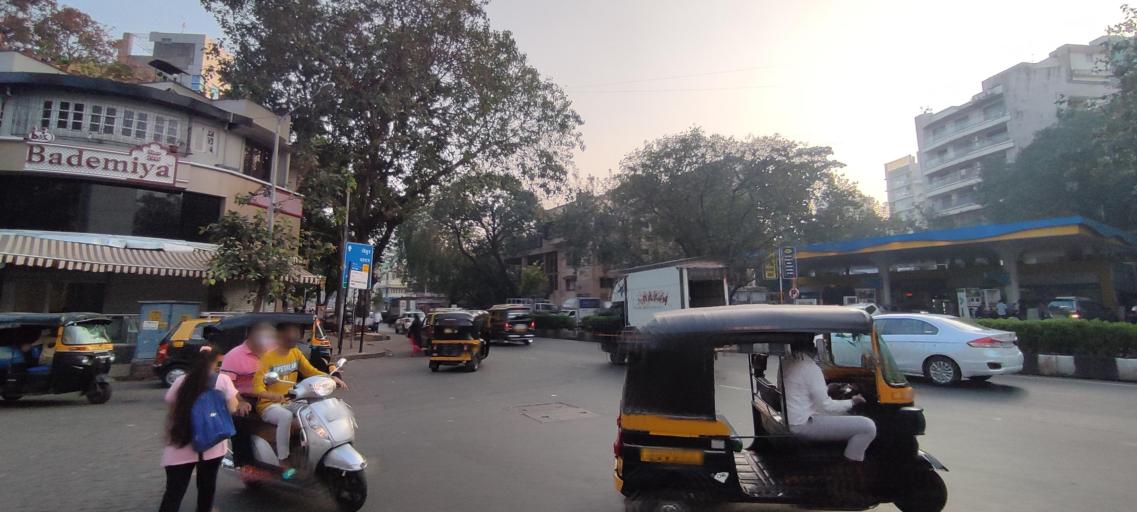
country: IN
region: Maharashtra
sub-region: Mumbai Suburban
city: Mumbai
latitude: 19.0618
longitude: 72.8360
